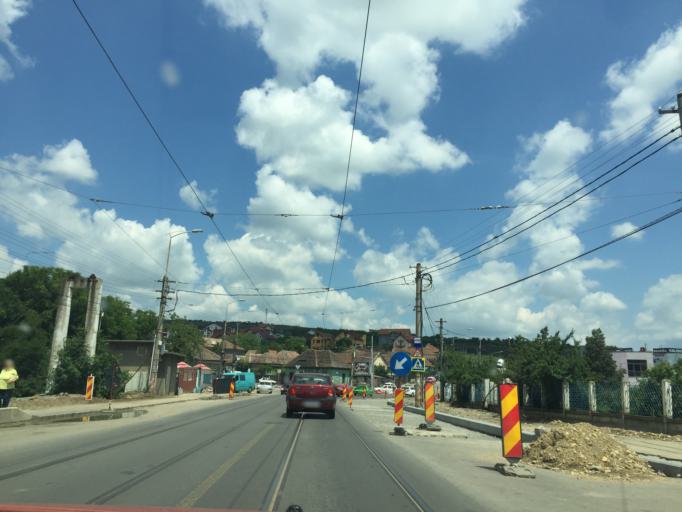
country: RO
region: Cluj
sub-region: Municipiul Cluj-Napoca
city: Cluj-Napoca
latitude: 46.7985
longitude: 23.6067
